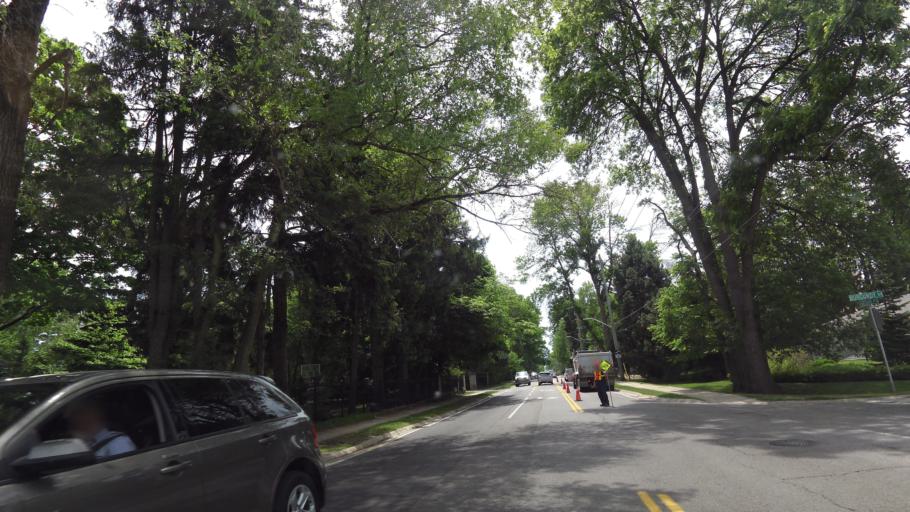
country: CA
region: Ontario
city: Oakville
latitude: 43.4579
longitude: -79.6552
